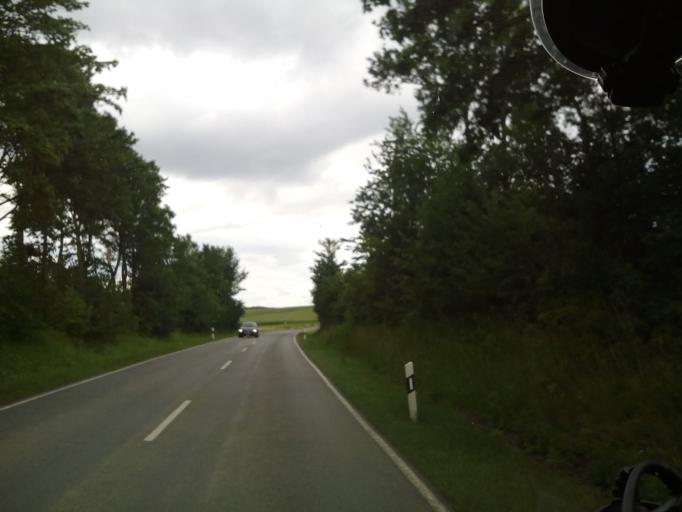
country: DE
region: Bavaria
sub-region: Upper Franconia
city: Sonnefeld
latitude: 50.2497
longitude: 11.0851
